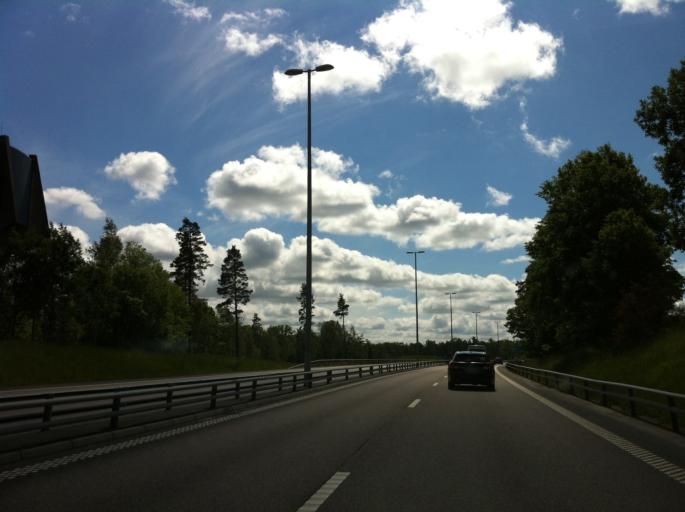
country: SE
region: Vaestra Goetaland
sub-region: Trollhattan
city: Trollhattan
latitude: 58.2540
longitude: 12.2798
